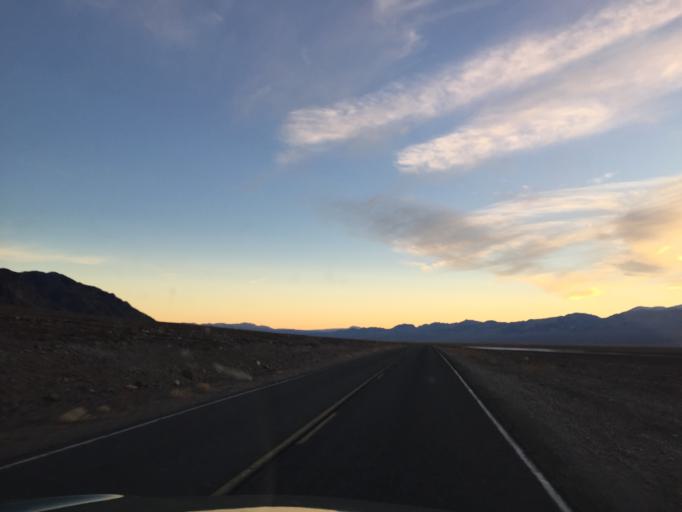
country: US
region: Nevada
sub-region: Nye County
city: Beatty
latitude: 36.2109
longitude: -116.7755
